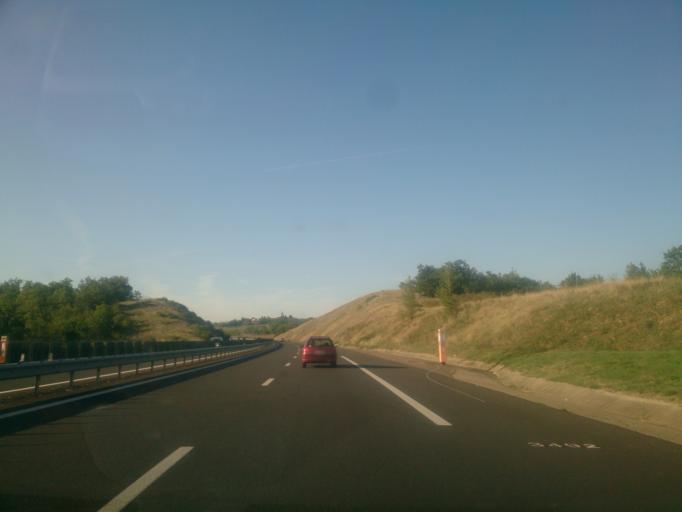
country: FR
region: Midi-Pyrenees
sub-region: Departement du Lot
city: Cahors
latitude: 44.5501
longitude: 1.5171
